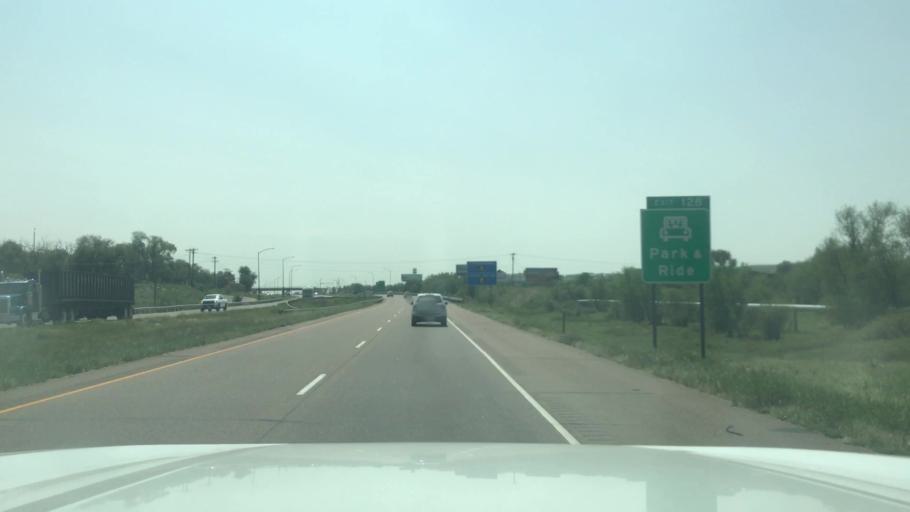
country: US
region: Colorado
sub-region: El Paso County
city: Fountain
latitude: 38.6809
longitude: -104.7145
